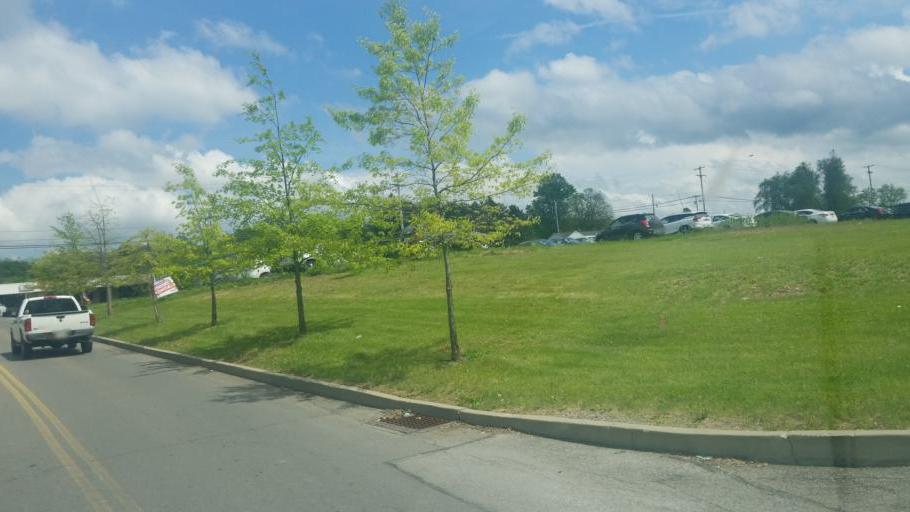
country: US
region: Pennsylvania
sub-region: Mercer County
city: Hermitage
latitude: 41.2470
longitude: -80.4510
